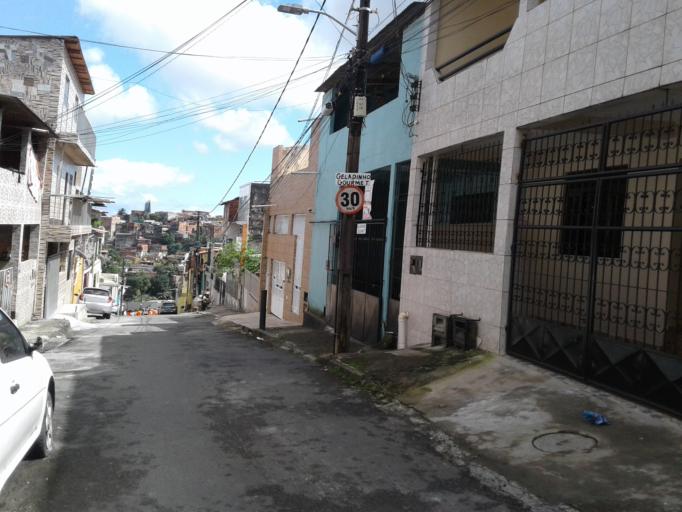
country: BR
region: Bahia
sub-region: Salvador
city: Salvador
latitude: -12.9125
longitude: -38.4712
